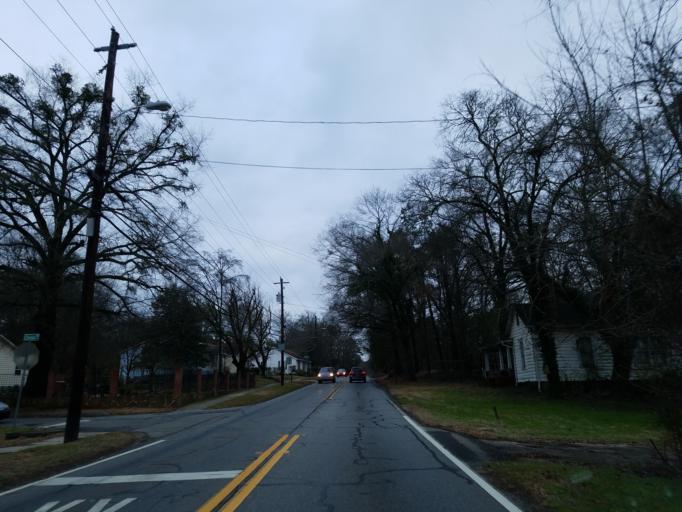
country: US
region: Georgia
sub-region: Bartow County
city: Cartersville
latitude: 34.1731
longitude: -84.8091
